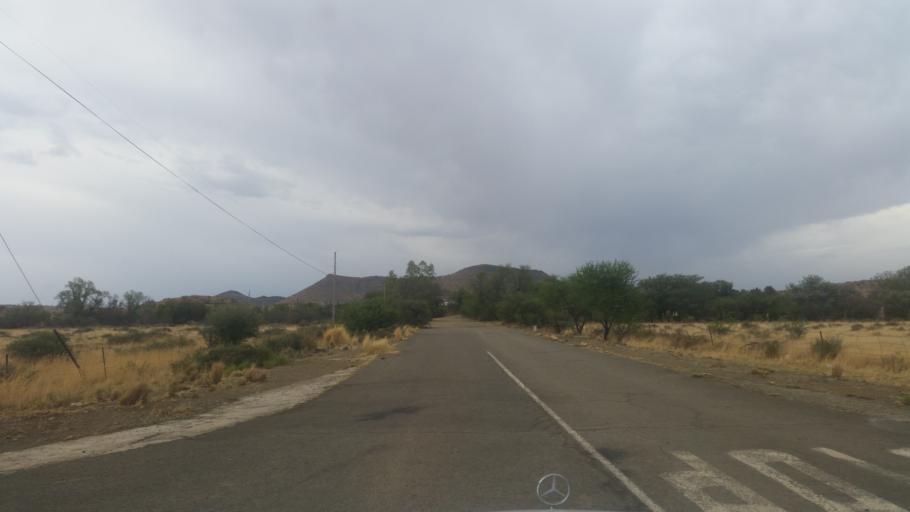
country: ZA
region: Orange Free State
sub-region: Xhariep District Municipality
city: Trompsburg
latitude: -30.4938
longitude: 25.9967
